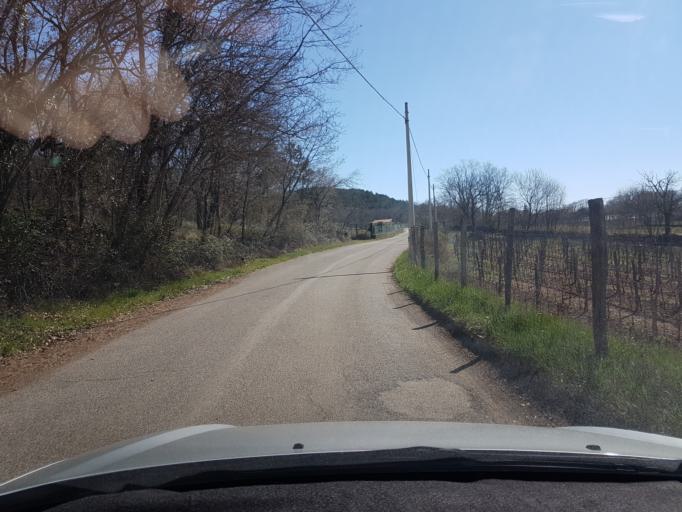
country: IT
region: Friuli Venezia Giulia
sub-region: Provincia di Trieste
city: Sgonico
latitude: 45.7528
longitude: 13.7237
